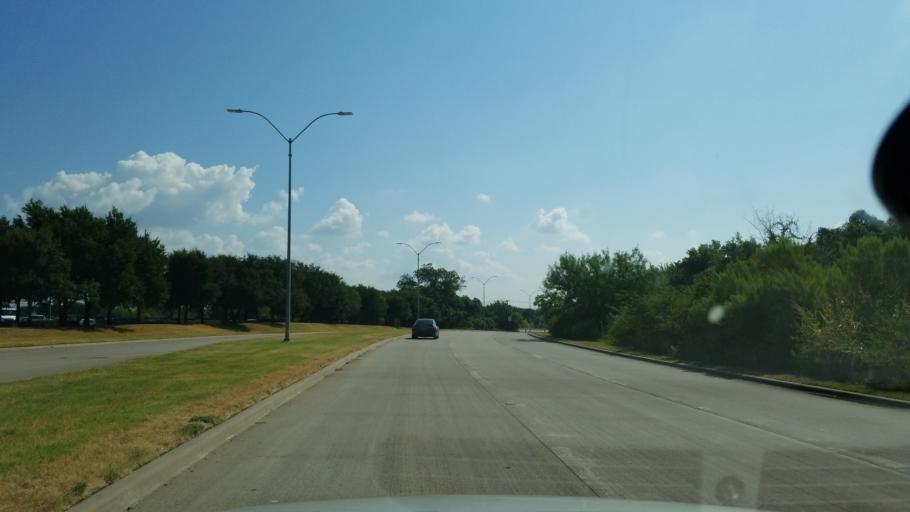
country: US
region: Texas
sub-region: Tarrant County
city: Euless
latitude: 32.8161
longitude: -97.1027
